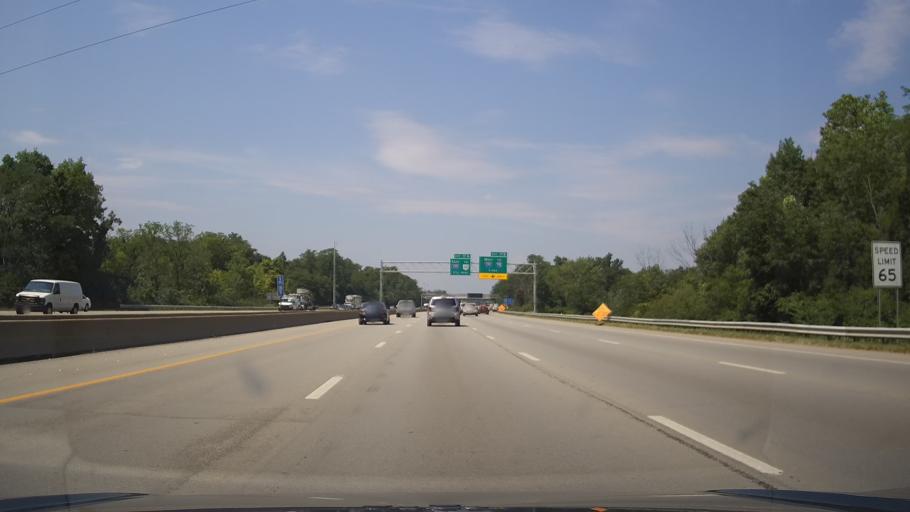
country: US
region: Ohio
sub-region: Hamilton County
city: Sixteen Mile Stand
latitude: 39.2835
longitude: -84.3299
